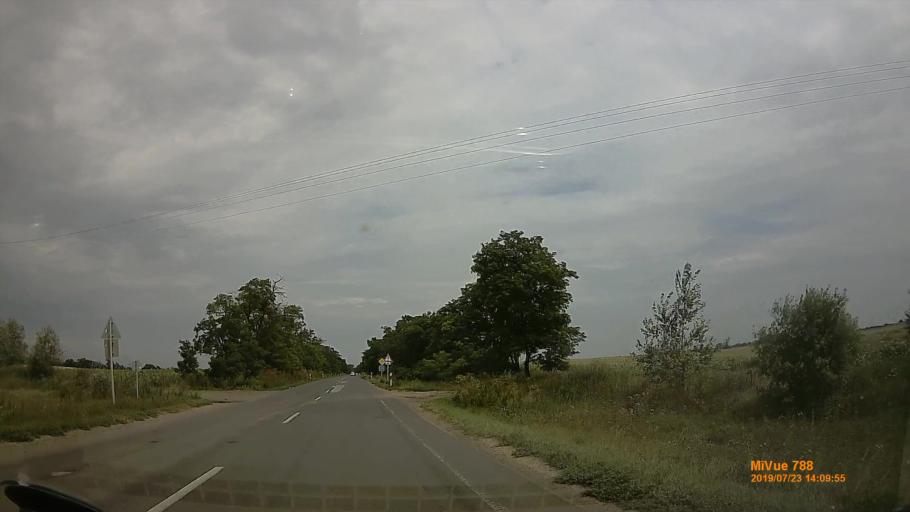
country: HU
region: Szabolcs-Szatmar-Bereg
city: Tiszavasvari
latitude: 47.9584
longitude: 21.4062
